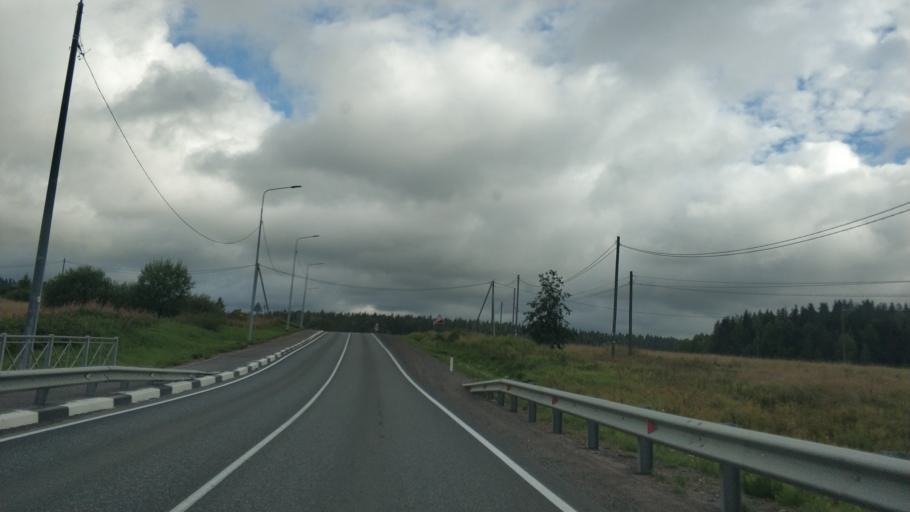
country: RU
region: Republic of Karelia
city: Khelyulya
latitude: 61.7580
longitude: 30.6572
